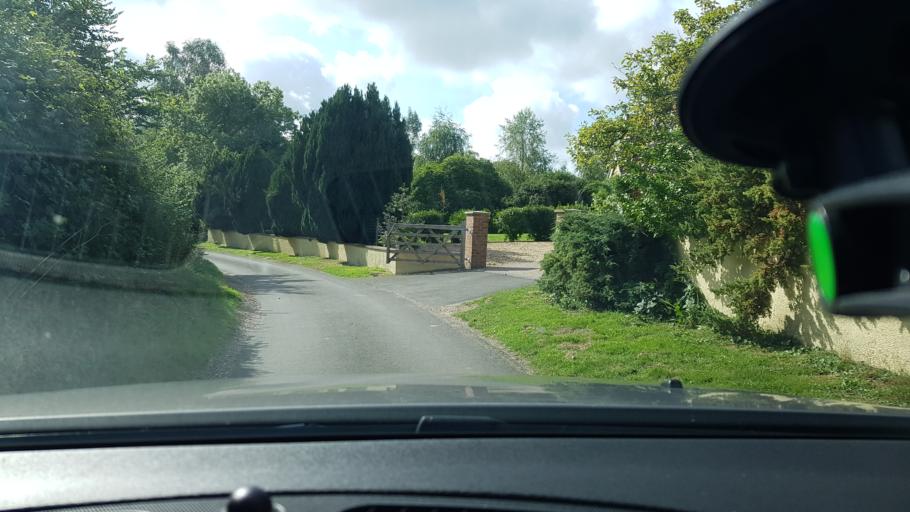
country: GB
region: England
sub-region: Hampshire
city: Highclere
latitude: 51.3359
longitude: -1.3376
